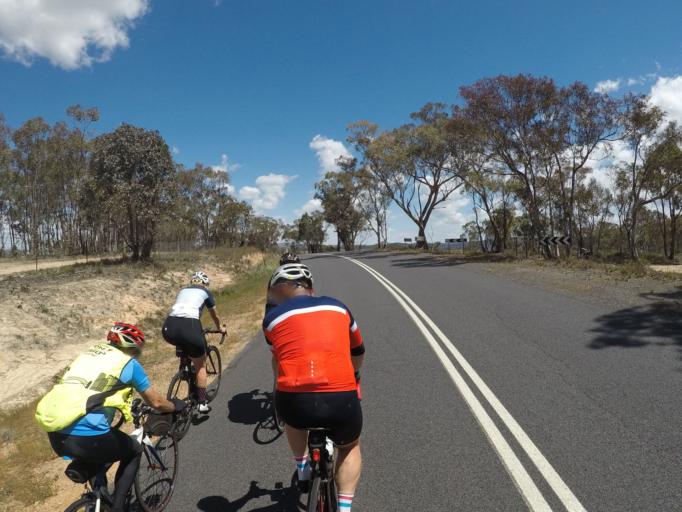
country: AU
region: New South Wales
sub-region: Bathurst Regional
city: Perthville
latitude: -33.5303
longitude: 149.4491
